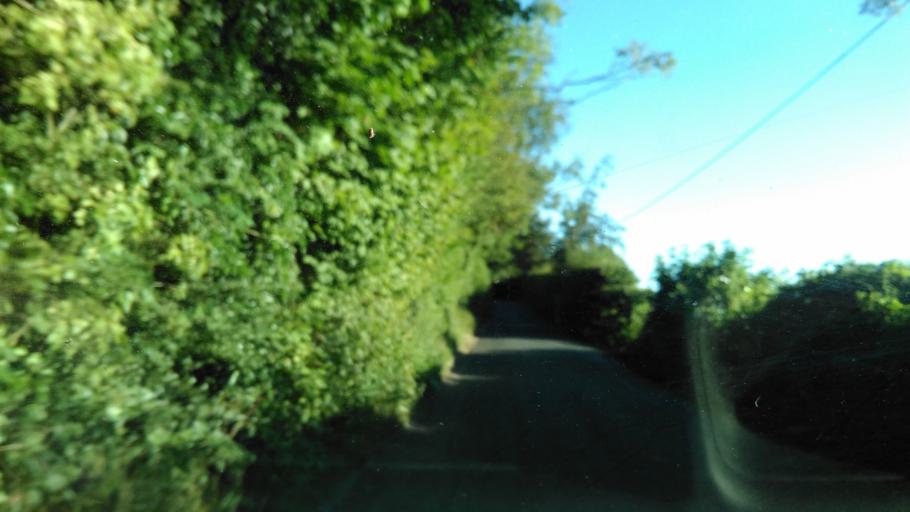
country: GB
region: England
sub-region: Kent
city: Chartham
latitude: 51.2767
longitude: 1.0115
